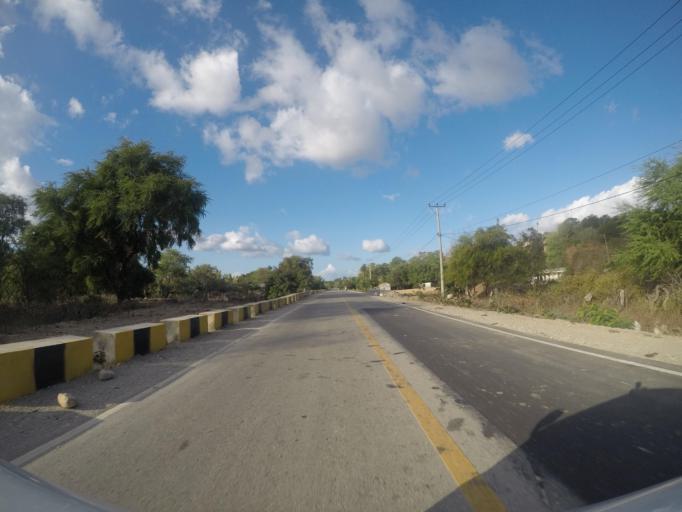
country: TL
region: Lautem
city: Lospalos
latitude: -8.3676
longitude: 126.8968
